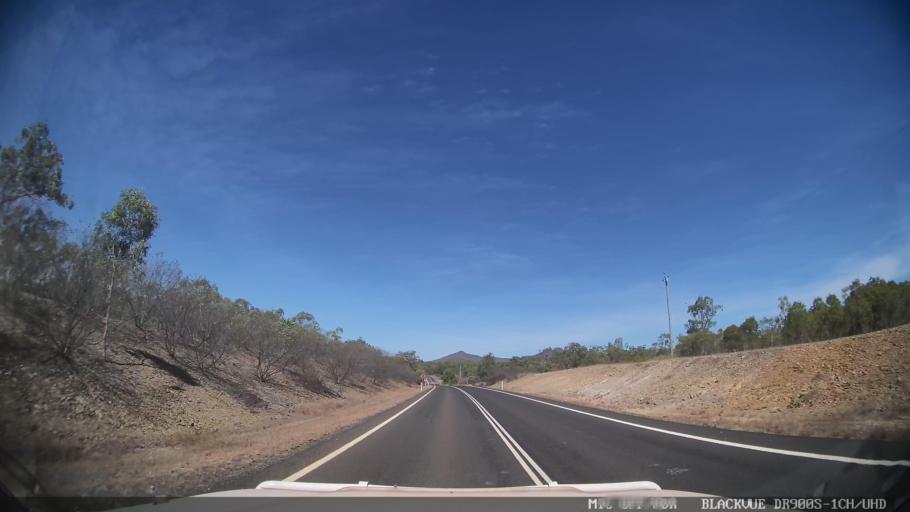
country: AU
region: Queensland
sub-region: Cook
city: Cooktown
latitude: -15.7093
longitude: 144.6123
